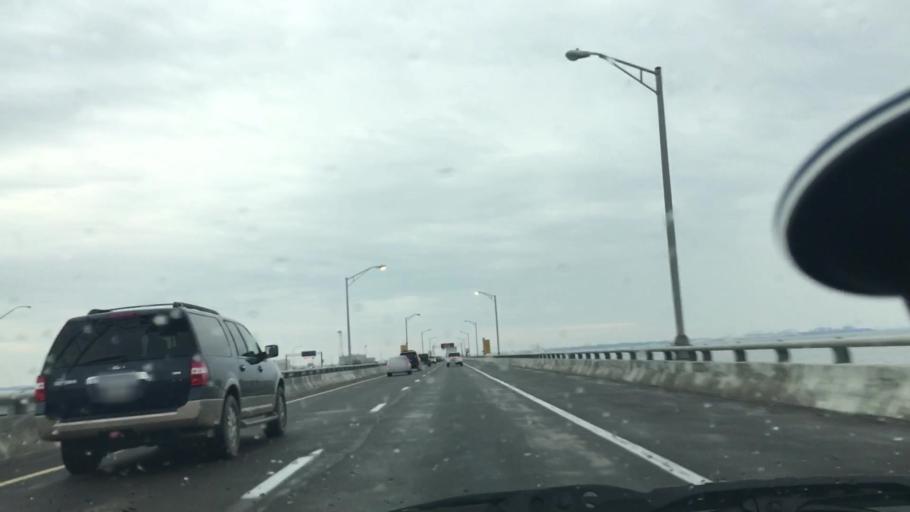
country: US
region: Virginia
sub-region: City of Hampton
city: East Hampton
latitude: 37.0071
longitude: -76.3215
